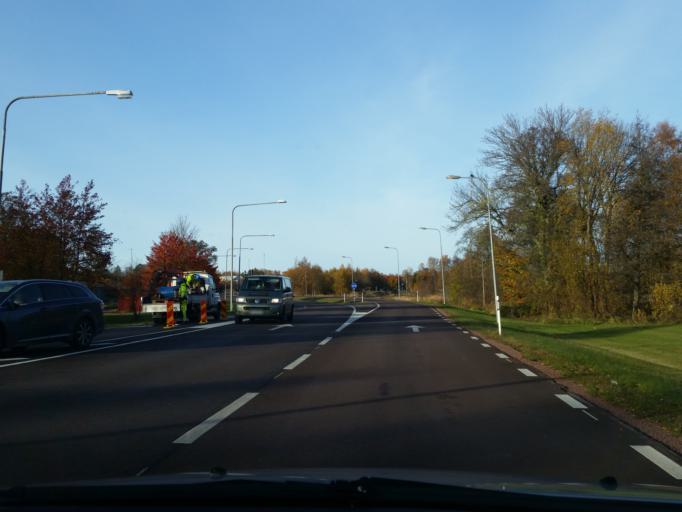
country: AX
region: Mariehamns stad
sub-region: Mariehamn
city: Mariehamn
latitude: 60.1112
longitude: 19.9431
